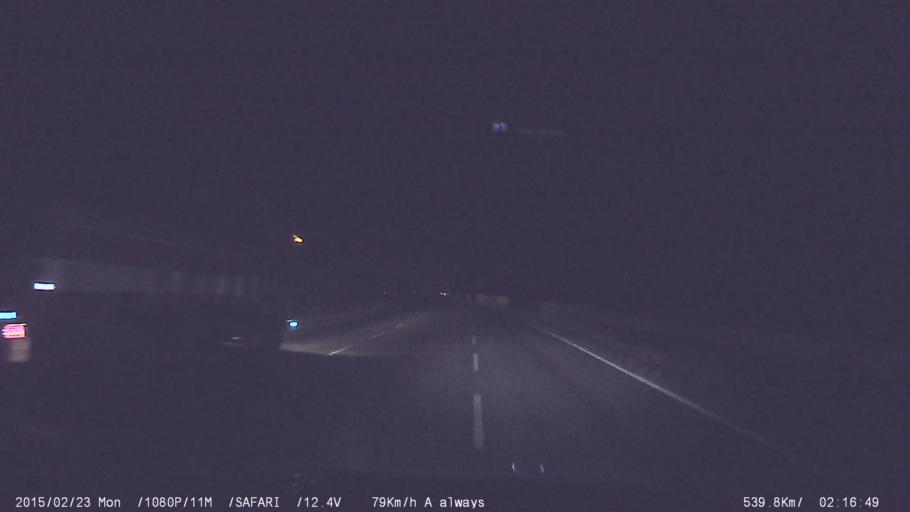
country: IN
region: Tamil Nadu
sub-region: Krishnagiri
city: Hosur
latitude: 12.7005
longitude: 77.9095
